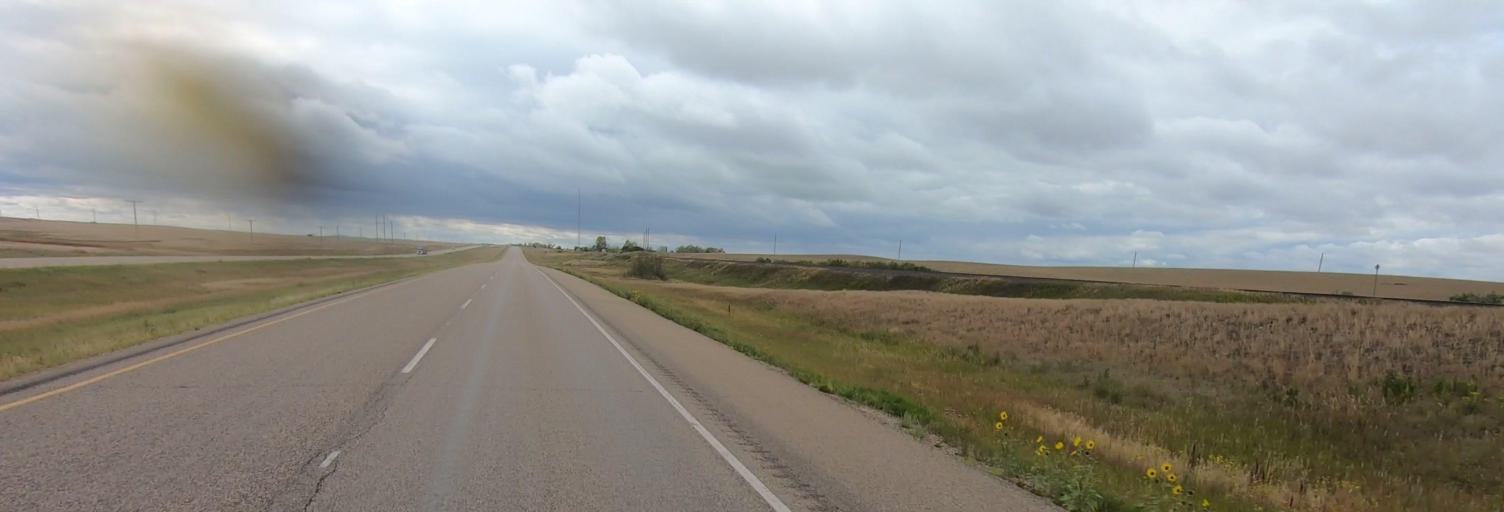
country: CA
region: Saskatchewan
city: Gravelbourg
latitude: 50.4230
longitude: -106.9336
